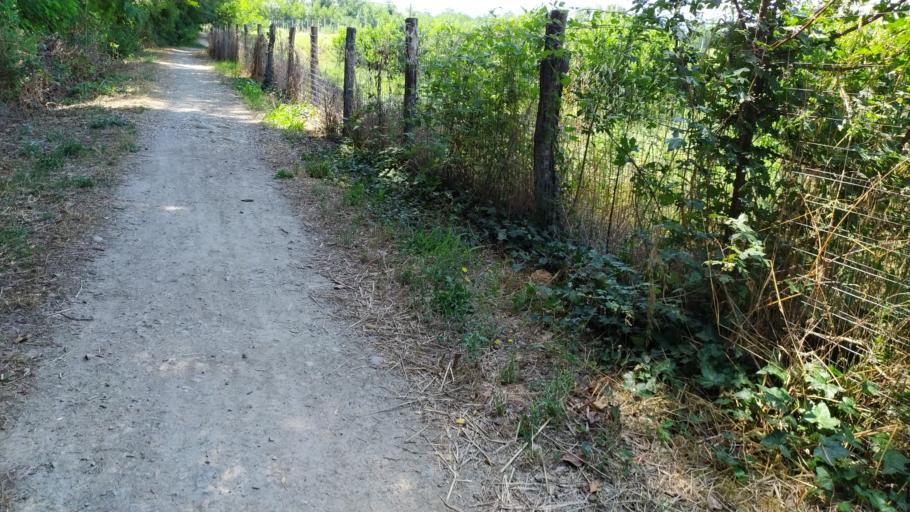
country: IT
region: Emilia-Romagna
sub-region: Forli-Cesena
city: Castrocaro Terme e Terra del Sole
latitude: 44.2018
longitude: 11.9976
